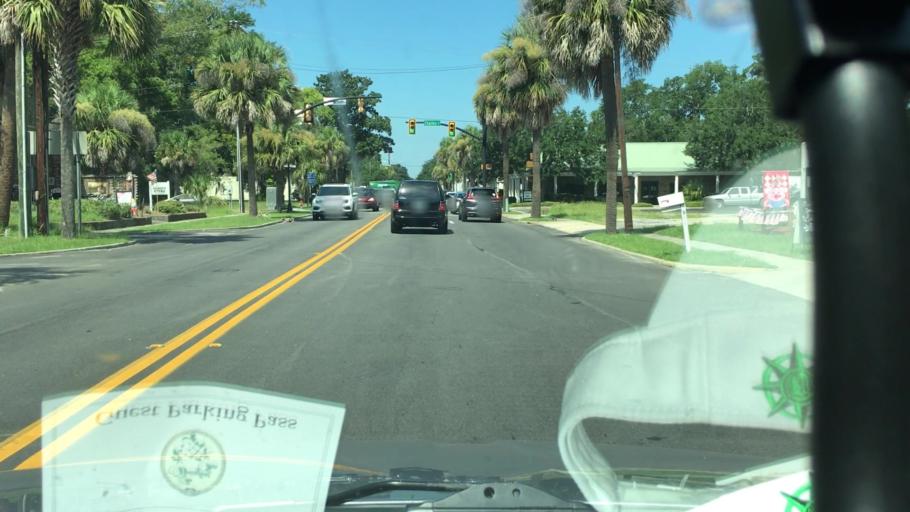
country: US
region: South Carolina
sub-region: Beaufort County
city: Beaufort
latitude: 32.4396
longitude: -80.6721
